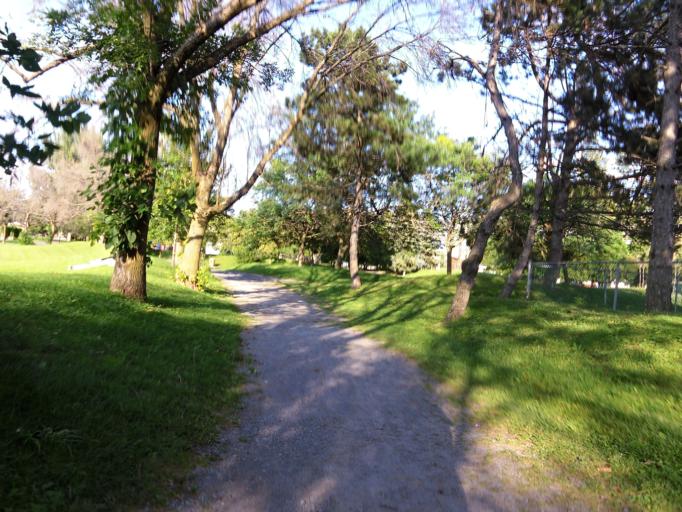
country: CA
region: Ontario
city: Ottawa
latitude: 45.4307
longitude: -75.7167
